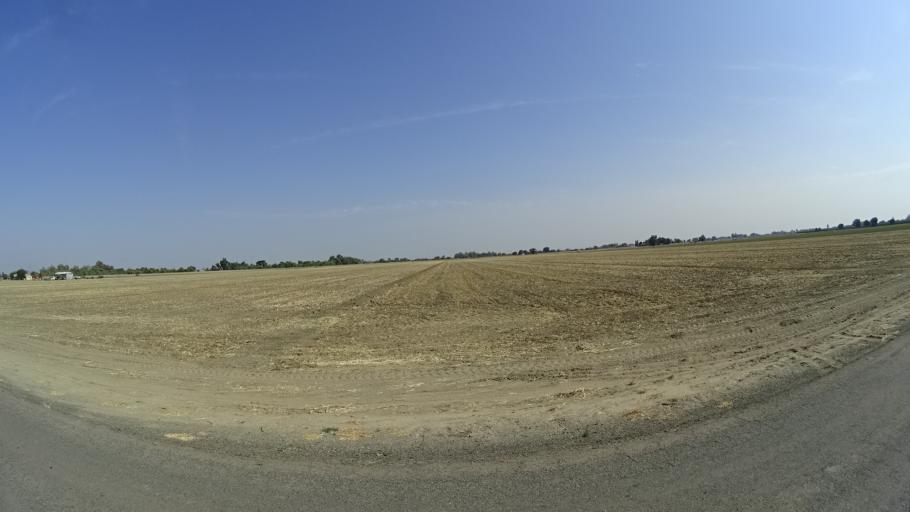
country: US
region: California
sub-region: Kings County
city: Lemoore Station
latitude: 36.3277
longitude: -119.8702
